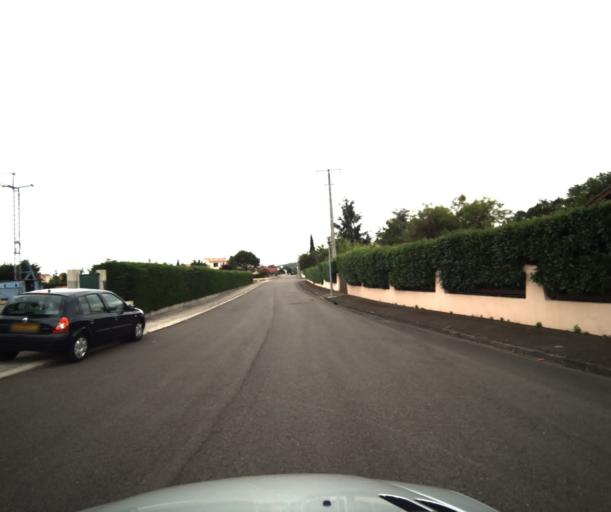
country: FR
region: Midi-Pyrenees
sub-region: Departement de la Haute-Garonne
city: Lacroix-Falgarde
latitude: 43.4921
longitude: 1.3981
